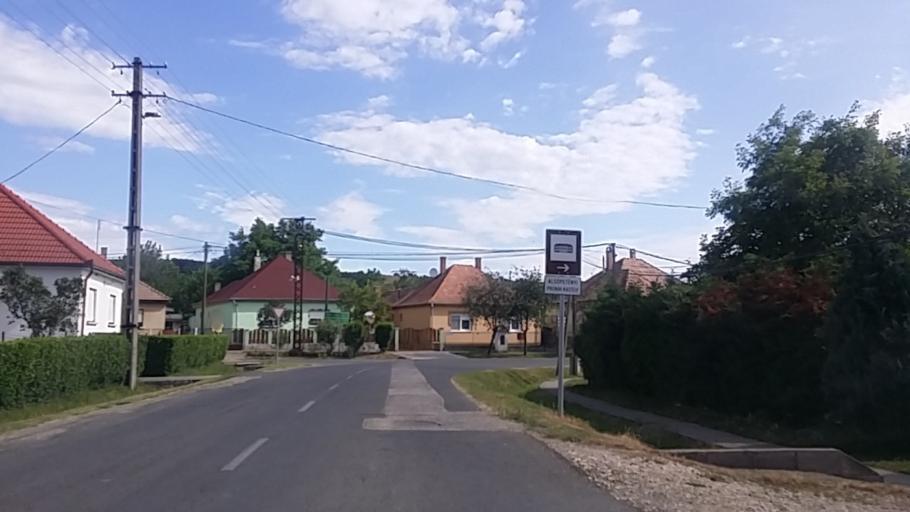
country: HU
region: Pest
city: Kosd
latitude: 47.8367
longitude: 19.2347
